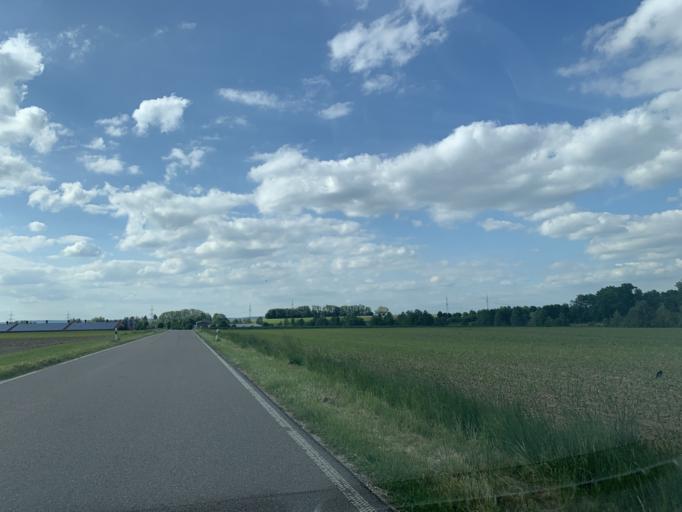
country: DE
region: Baden-Wuerttemberg
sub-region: Tuebingen Region
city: Huttisheim
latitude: 48.2870
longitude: 9.9357
